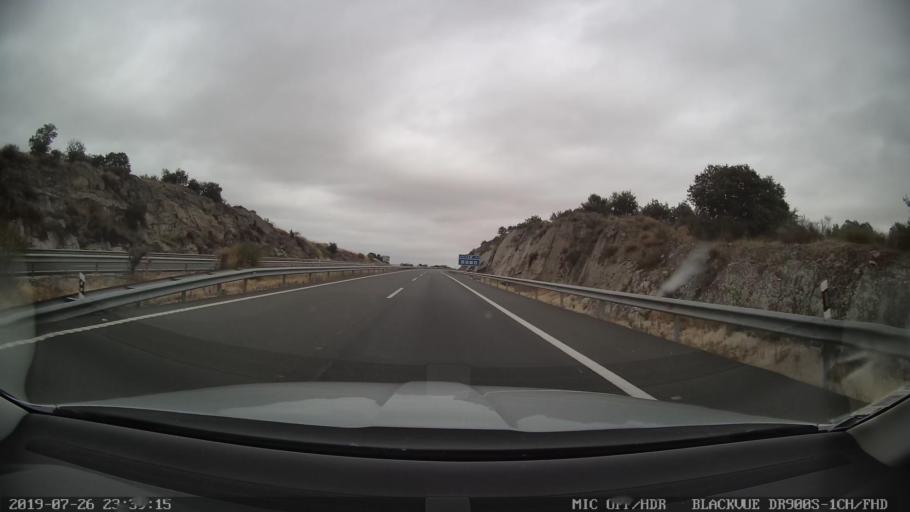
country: ES
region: Extremadura
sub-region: Provincia de Caceres
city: Trujillo
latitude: 39.4452
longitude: -5.8743
